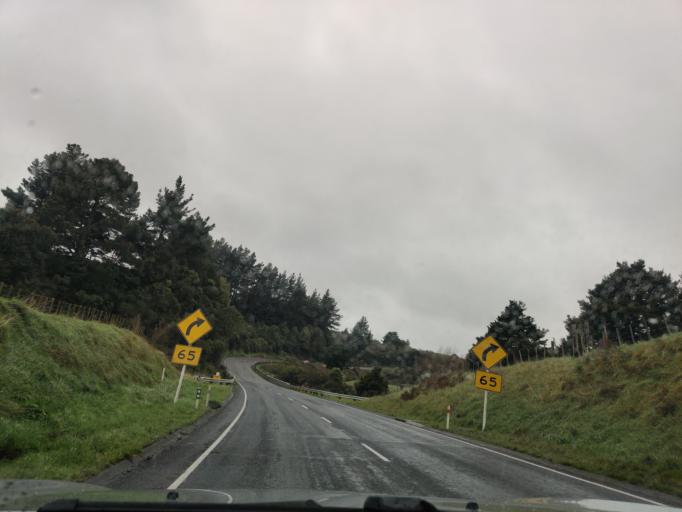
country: NZ
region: Manawatu-Wanganui
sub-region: Palmerston North City
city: Palmerston North
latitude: -40.0539
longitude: 176.2385
